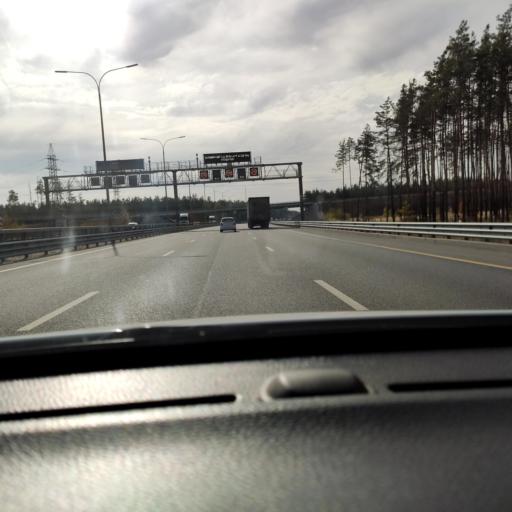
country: RU
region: Voronezj
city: Somovo
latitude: 51.7292
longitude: 39.3112
